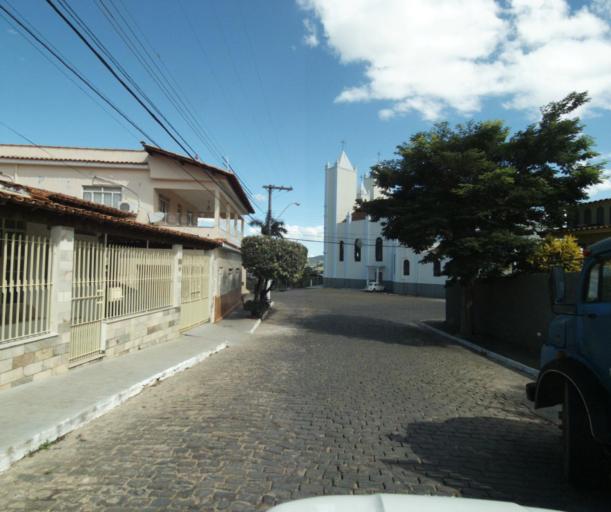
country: BR
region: Espirito Santo
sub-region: Sao Jose Do Calcado
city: Sao Jose do Calcado
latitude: -21.0245
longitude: -41.6546
